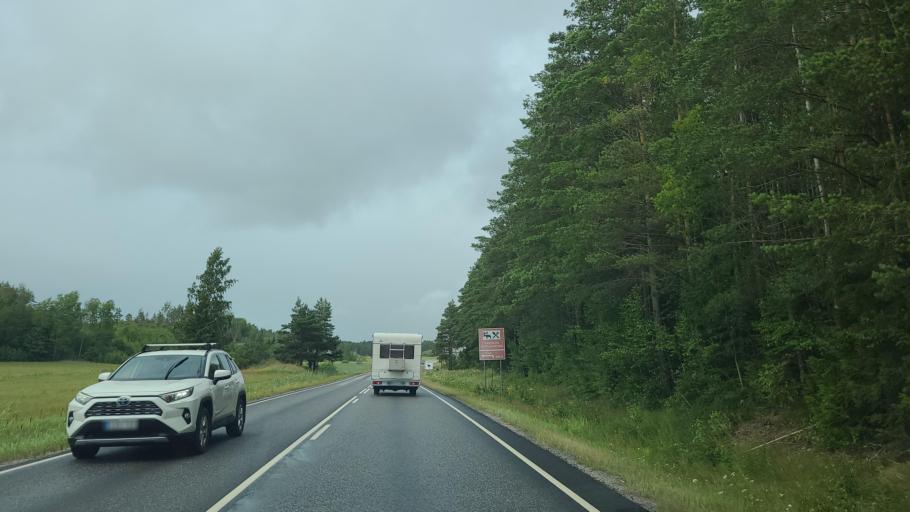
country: FI
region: Varsinais-Suomi
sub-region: Turku
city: Sauvo
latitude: 60.2525
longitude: 22.6240
